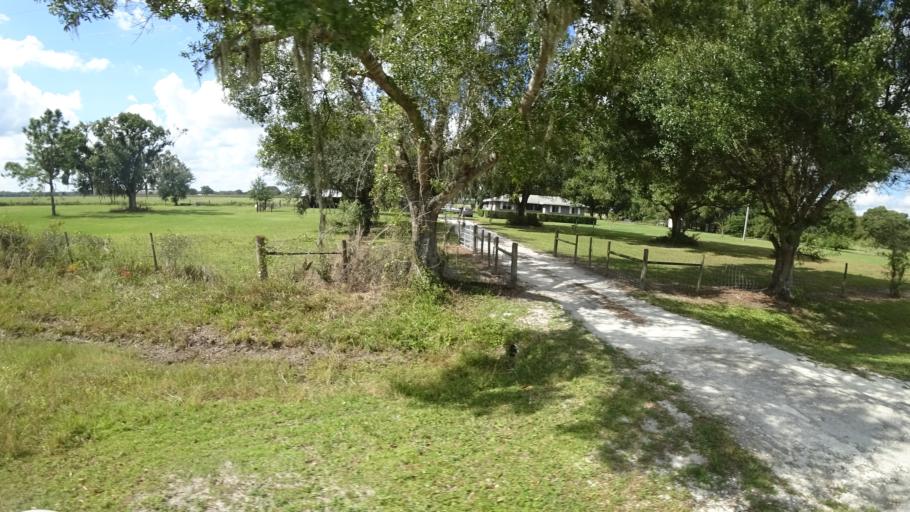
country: US
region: Florida
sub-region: Sarasota County
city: Warm Mineral Springs
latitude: 27.2612
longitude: -82.1208
